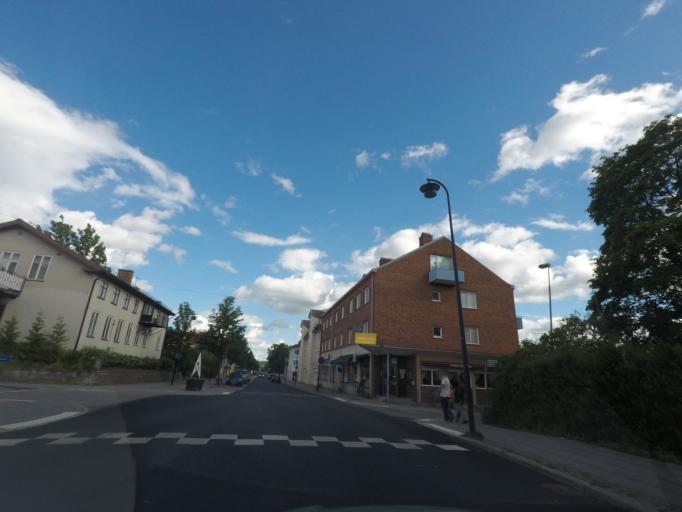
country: SE
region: OErebro
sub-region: Lindesbergs Kommun
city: Lindesberg
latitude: 59.5959
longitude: 15.2245
